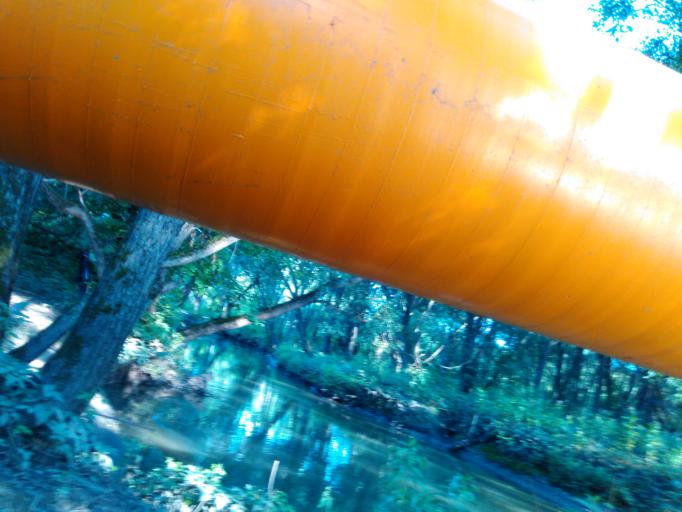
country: RU
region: Moskovskaya
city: Kastanayevo
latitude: 55.7200
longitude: 37.4957
